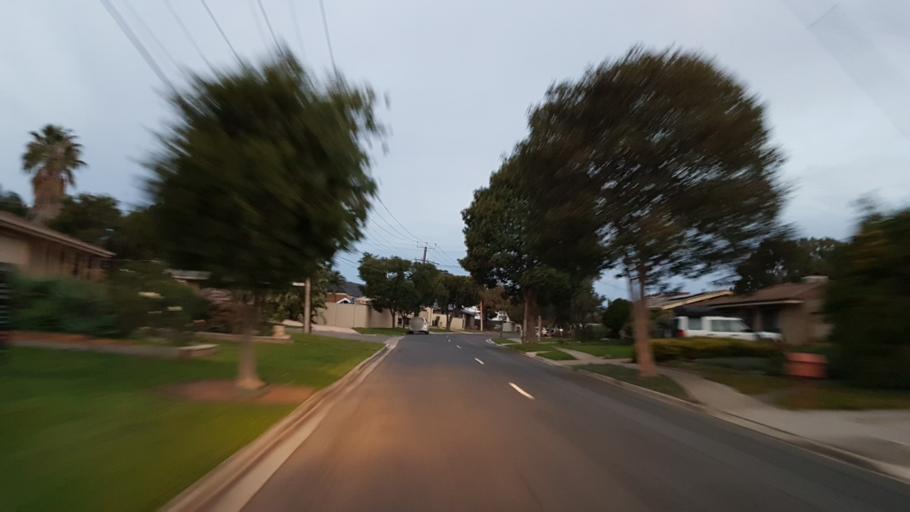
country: AU
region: South Australia
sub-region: Port Adelaide Enfield
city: Gilles Plains
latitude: -34.8468
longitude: 138.6670
